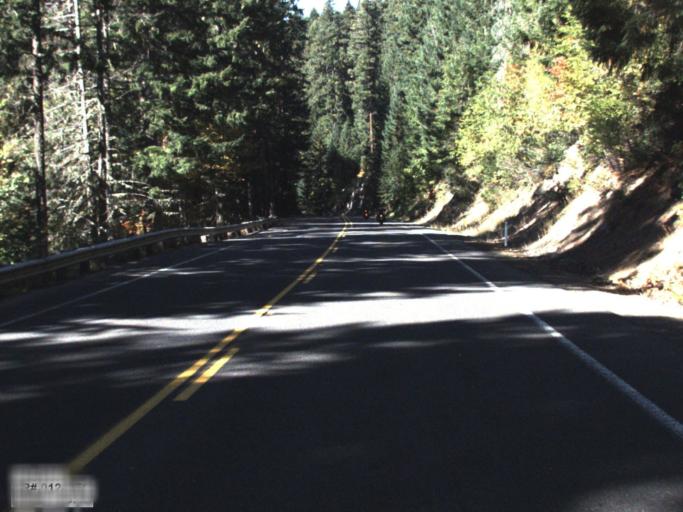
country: US
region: Washington
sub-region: Pierce County
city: Buckley
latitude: 46.6713
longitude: -121.4972
